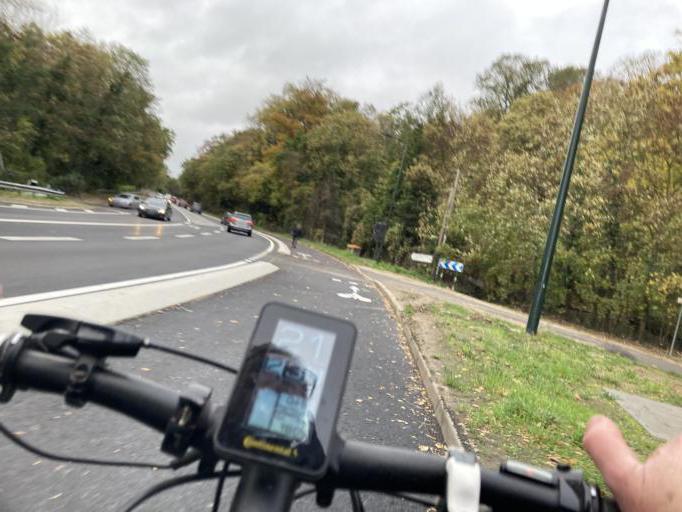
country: FR
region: Picardie
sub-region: Departement de l'Oise
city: Lamorlaye
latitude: 49.1622
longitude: 2.4483
